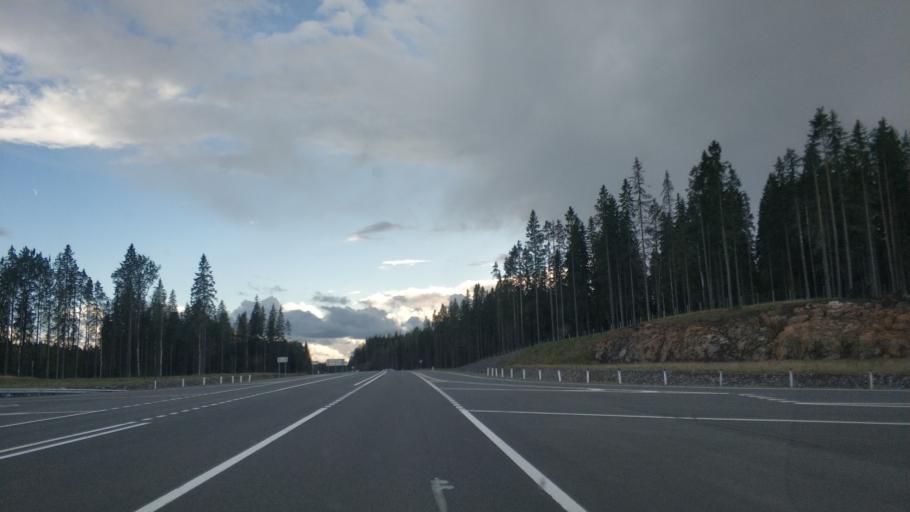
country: RU
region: Republic of Karelia
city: Lakhdenpokh'ya
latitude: 61.4652
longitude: 30.0006
